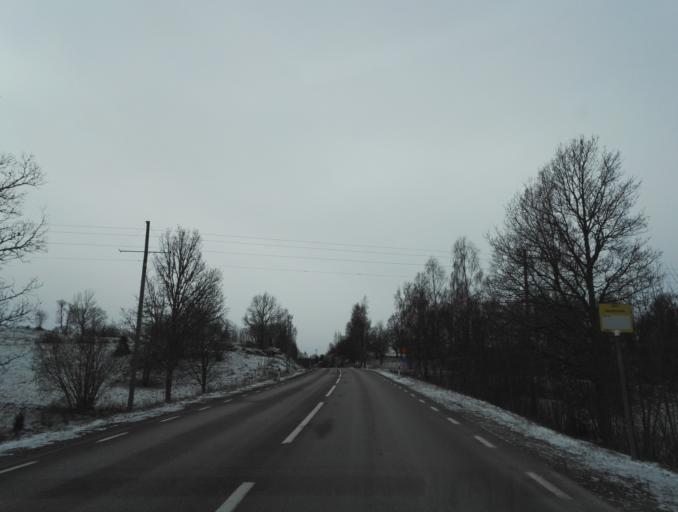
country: SE
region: Kalmar
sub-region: Hultsfreds Kommun
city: Virserum
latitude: 57.2950
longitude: 15.5677
